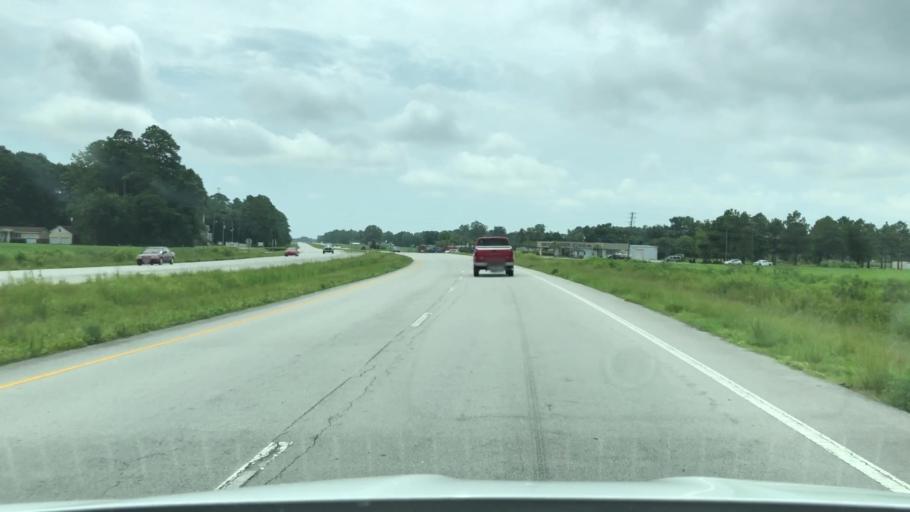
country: US
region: North Carolina
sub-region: Carteret County
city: Newport
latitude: 34.8136
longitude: -76.8799
